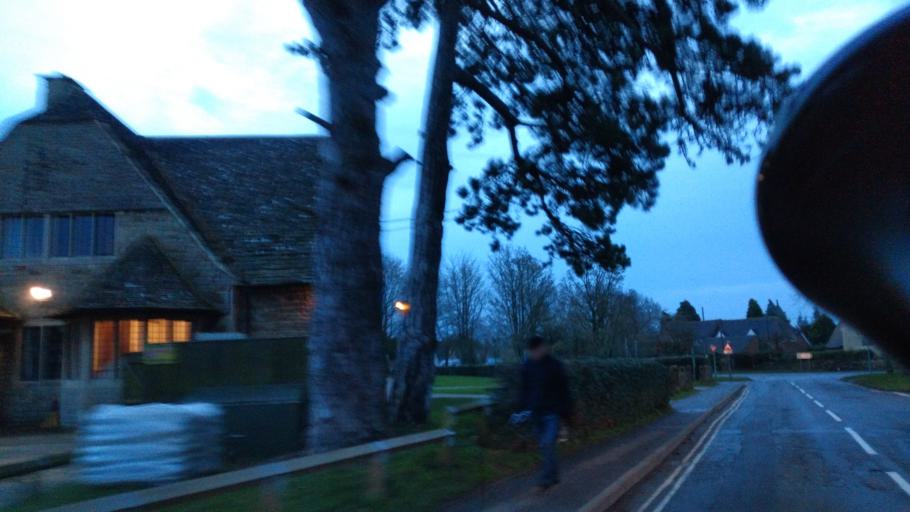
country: GB
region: England
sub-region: Oxfordshire
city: Shrivenham
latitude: 51.5982
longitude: -1.6588
